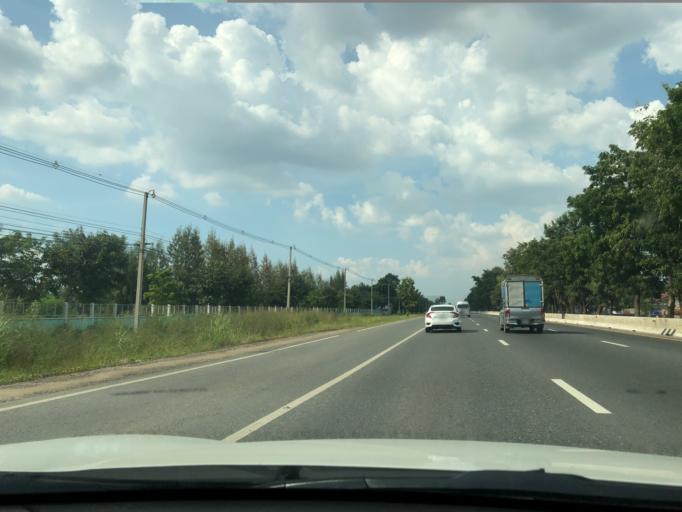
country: TH
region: Nakhon Sawan
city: Krok Phra
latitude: 15.5808
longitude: 100.1243
